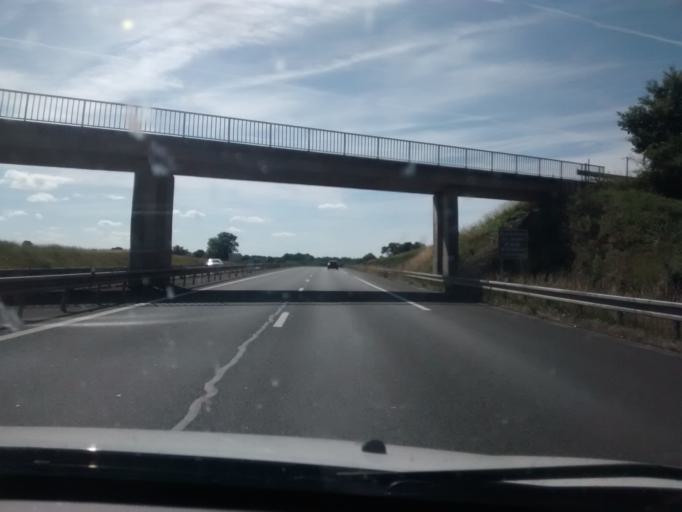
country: FR
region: Pays de la Loire
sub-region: Departement de la Mayenne
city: Vaiges
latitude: 48.0600
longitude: -0.5140
